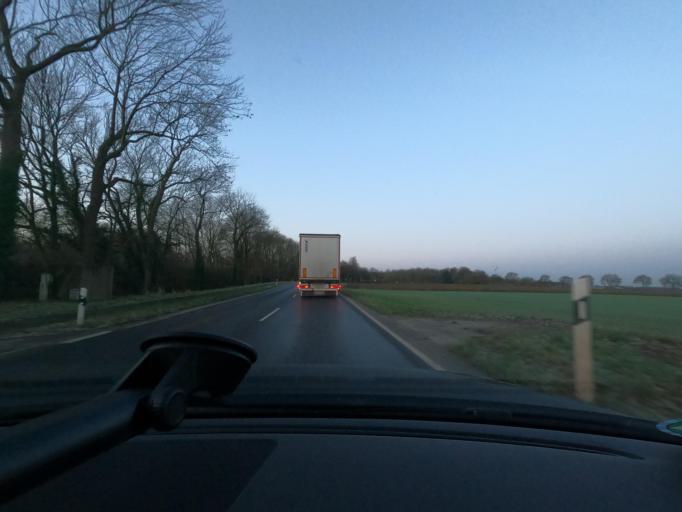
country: DE
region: North Rhine-Westphalia
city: Kempen
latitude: 51.3351
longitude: 6.4040
